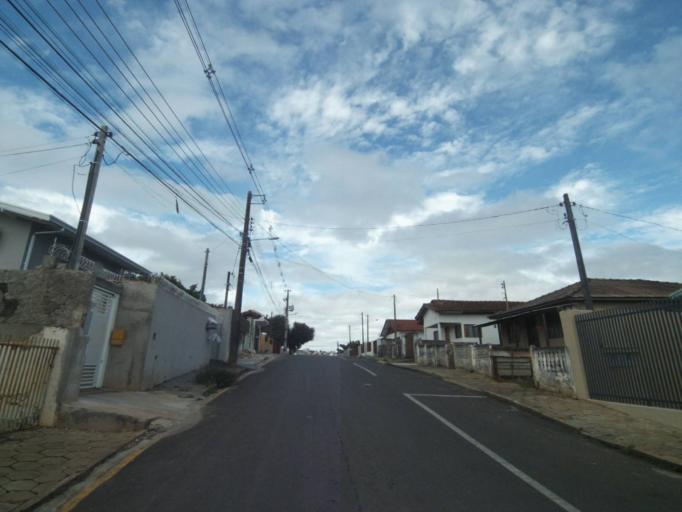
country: BR
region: Parana
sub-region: Telemaco Borba
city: Telemaco Borba
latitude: -24.3223
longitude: -50.6215
